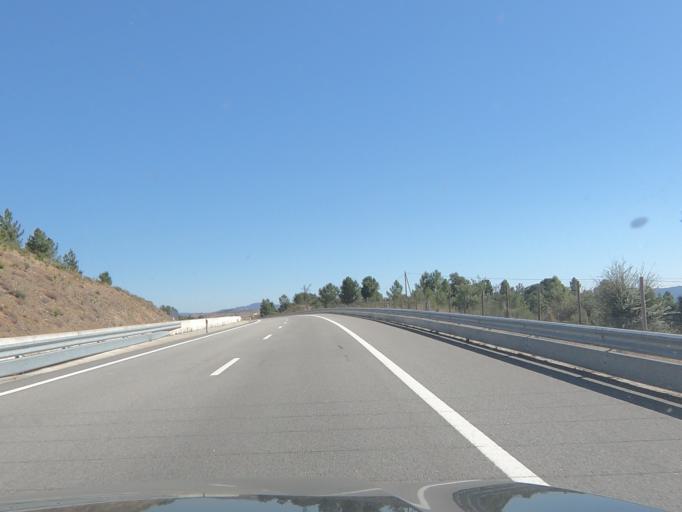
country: PT
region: Vila Real
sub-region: Murca
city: Murca
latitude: 41.4260
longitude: -7.3904
